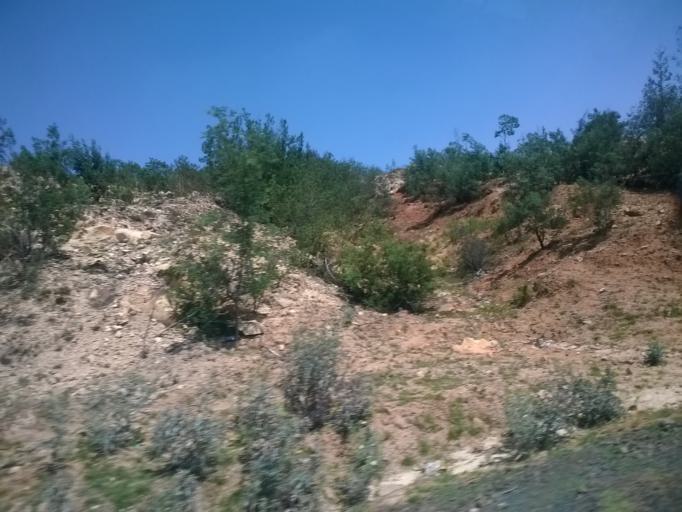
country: LS
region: Berea
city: Teyateyaneng
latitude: -29.1128
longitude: 27.8252
